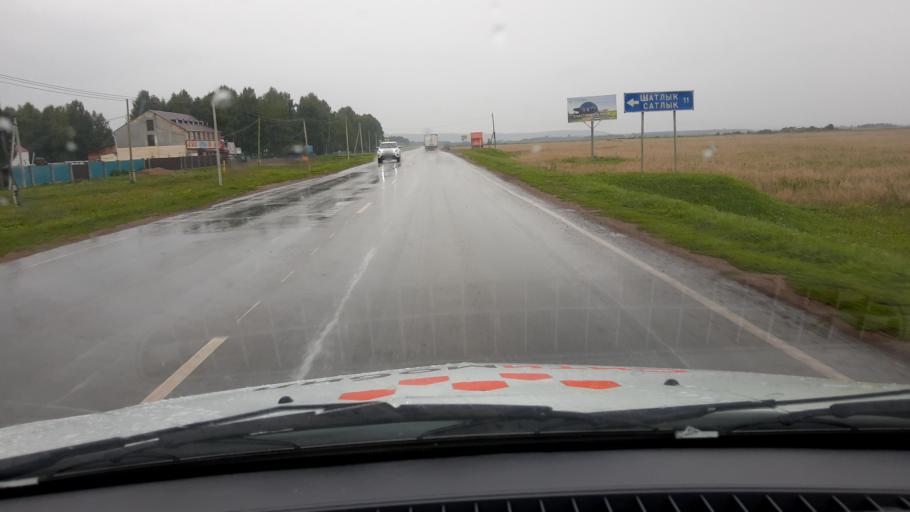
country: RU
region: Bashkortostan
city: Krasnaya Gorka
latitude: 55.0880
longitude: 56.6127
